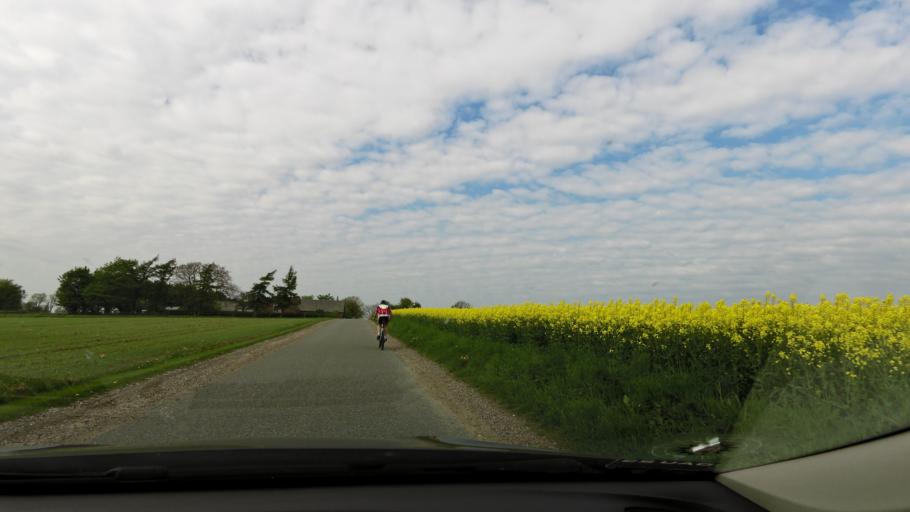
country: DK
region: South Denmark
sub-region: Nyborg Kommune
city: Nyborg
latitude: 55.2473
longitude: 10.7091
